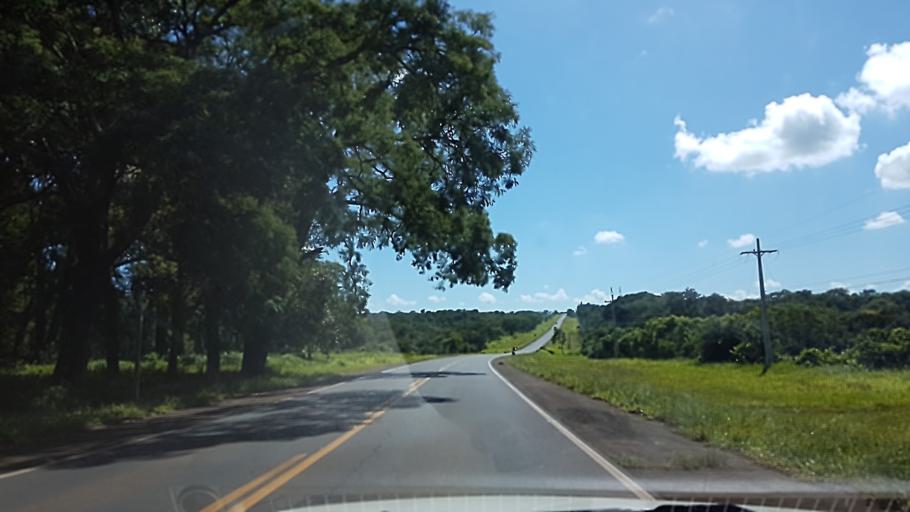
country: PY
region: Itapua
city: Carmen del Parana
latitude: -27.2113
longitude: -56.0839
